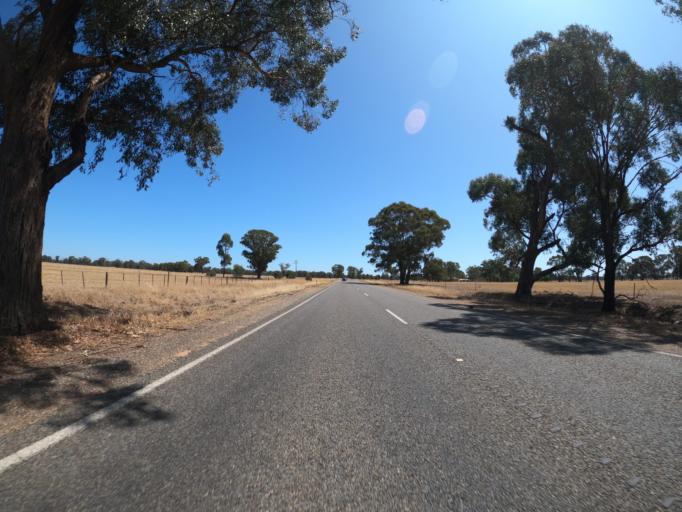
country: AU
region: New South Wales
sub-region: Corowa Shire
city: Corowa
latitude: -36.0757
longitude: 146.3472
